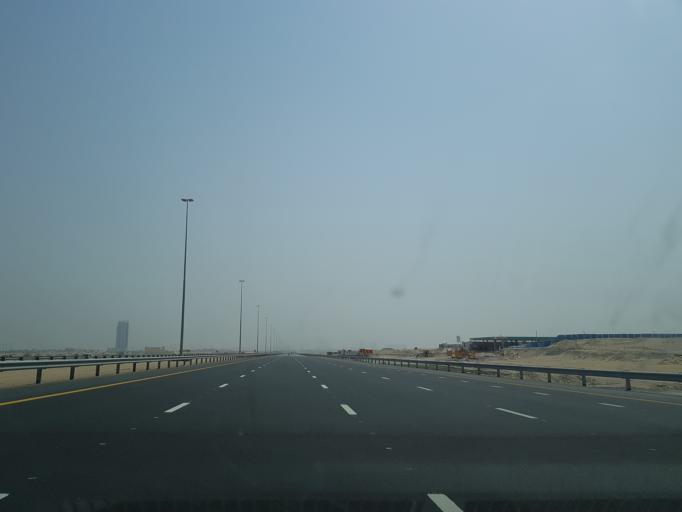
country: AE
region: Dubai
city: Dubai
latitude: 25.0640
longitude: 55.3114
